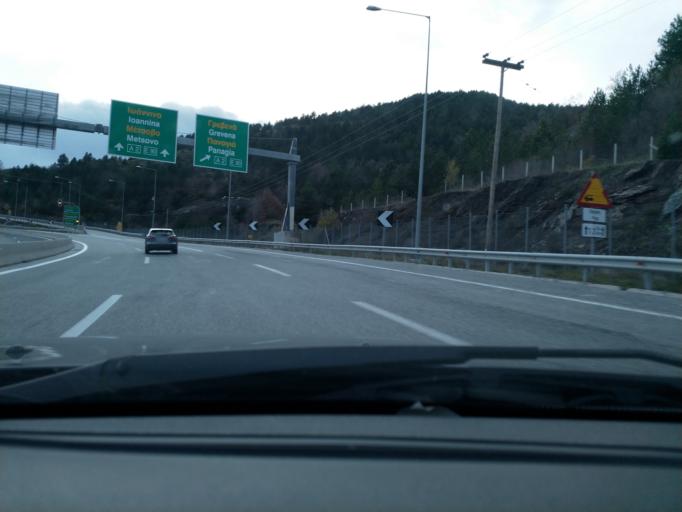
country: GR
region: Epirus
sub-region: Nomos Ioanninon
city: Metsovo
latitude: 39.7897
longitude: 21.2963
